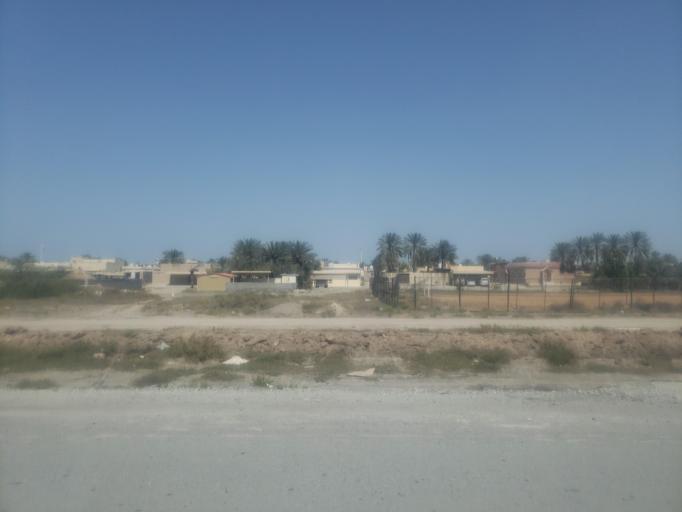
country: AE
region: Ra's al Khaymah
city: Ras al-Khaimah
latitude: 25.8750
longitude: 56.0309
